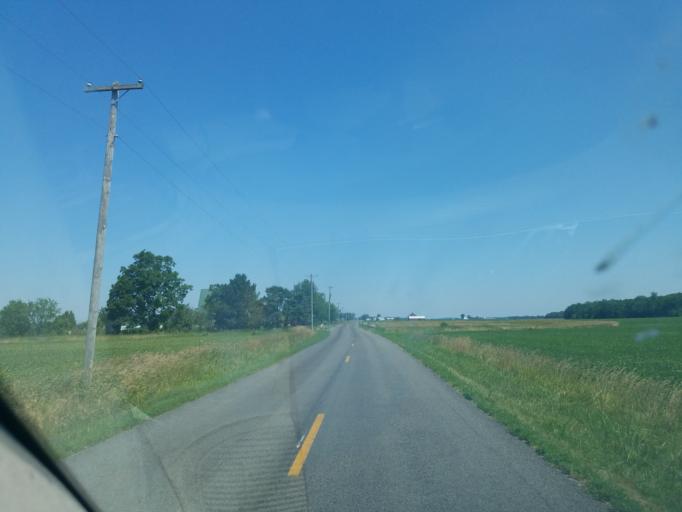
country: US
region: Ohio
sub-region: Mercer County
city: Rockford
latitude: 40.6397
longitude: -84.7086
